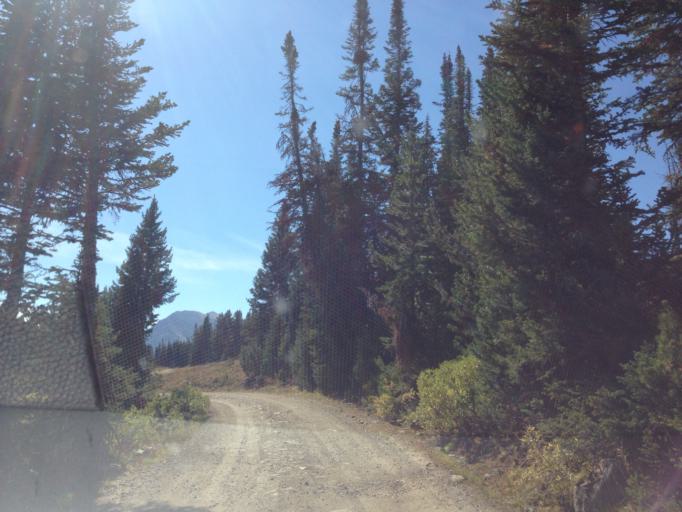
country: US
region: Montana
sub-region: Stillwater County
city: Absarokee
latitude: 45.0477
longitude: -109.9136
